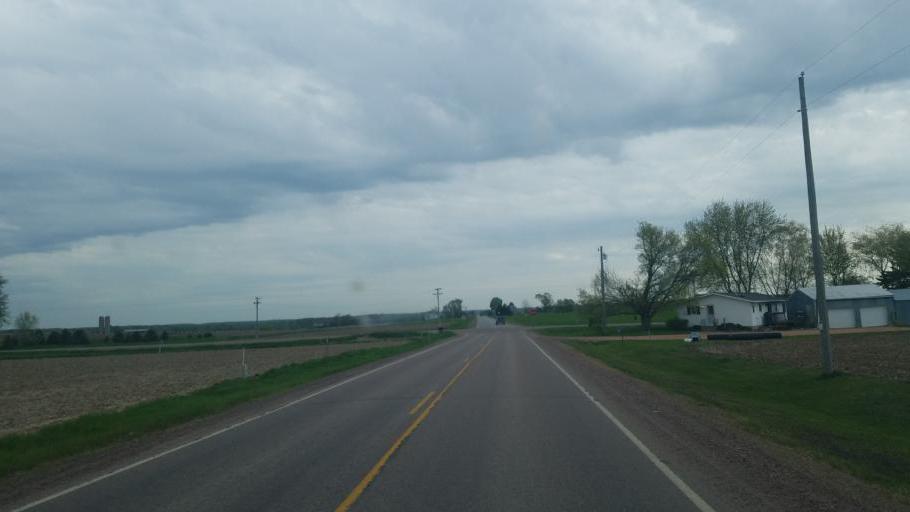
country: US
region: Wisconsin
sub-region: Wood County
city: Marshfield
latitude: 44.5978
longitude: -90.2986
